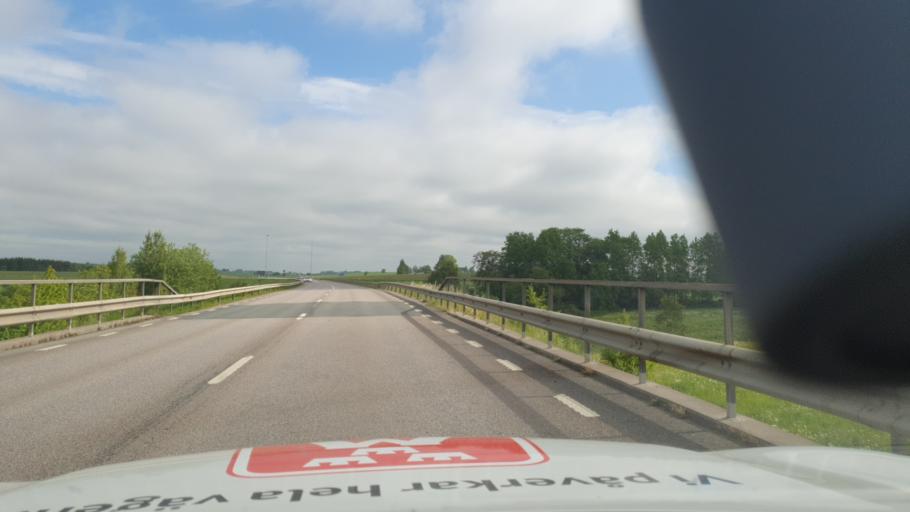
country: SE
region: Vaestra Goetaland
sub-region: Falkopings Kommun
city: Falkoeping
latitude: 58.1319
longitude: 13.5600
